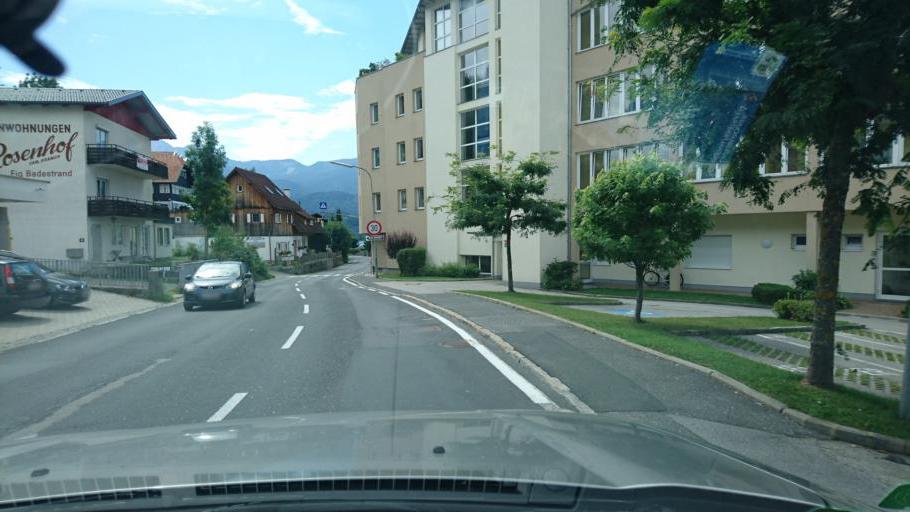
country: AT
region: Carinthia
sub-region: Politischer Bezirk Villach Land
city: Wernberg
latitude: 46.5852
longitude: 13.9335
